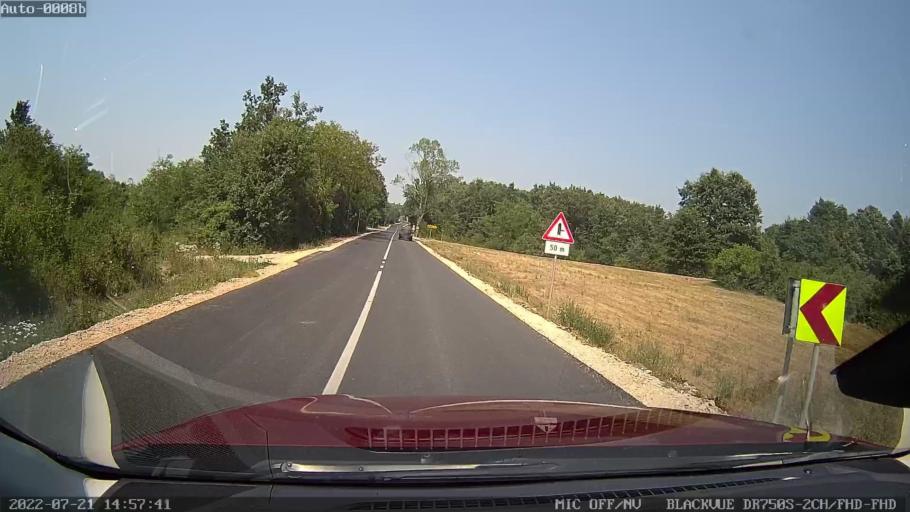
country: HR
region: Istarska
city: Pazin
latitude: 45.2104
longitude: 13.9541
